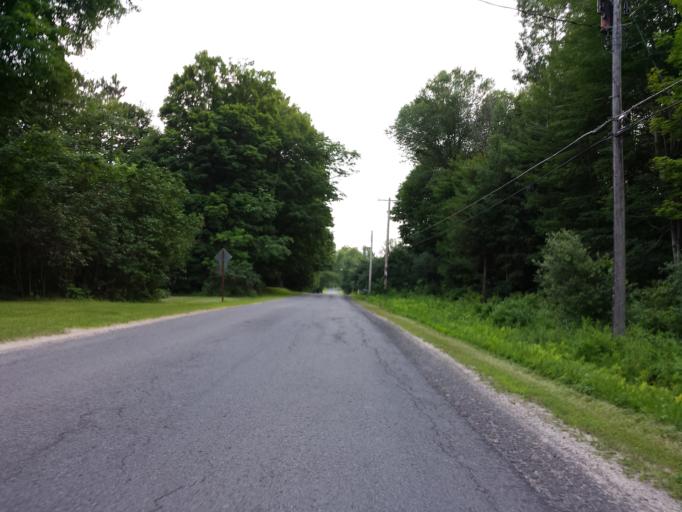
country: US
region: New York
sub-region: St. Lawrence County
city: Potsdam
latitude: 44.7121
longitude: -74.9027
